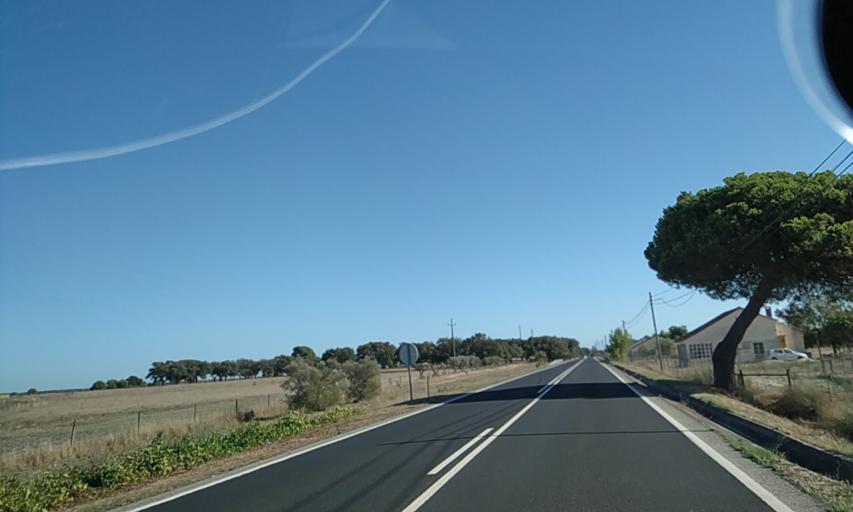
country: PT
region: Santarem
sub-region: Benavente
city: Poceirao
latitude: 38.8205
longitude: -8.8809
